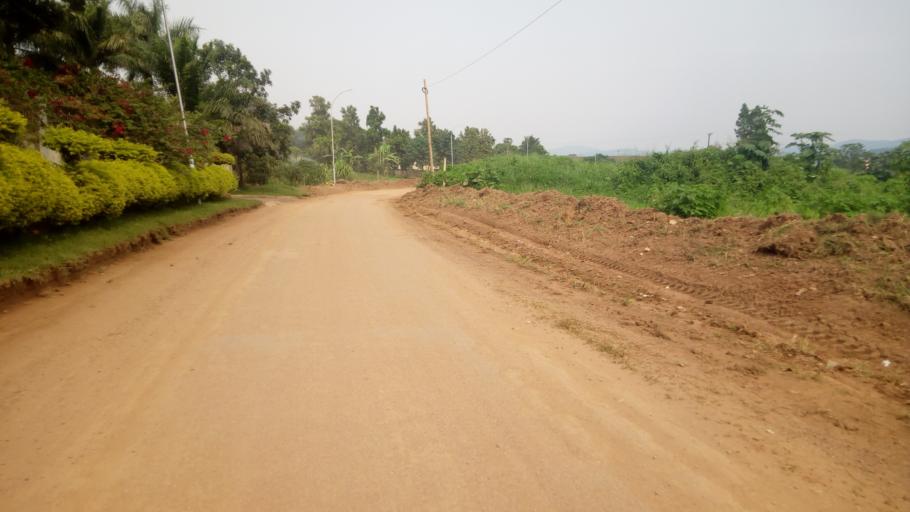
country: UG
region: Central Region
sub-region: Wakiso District
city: Kireka
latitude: 0.2931
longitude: 32.6577
